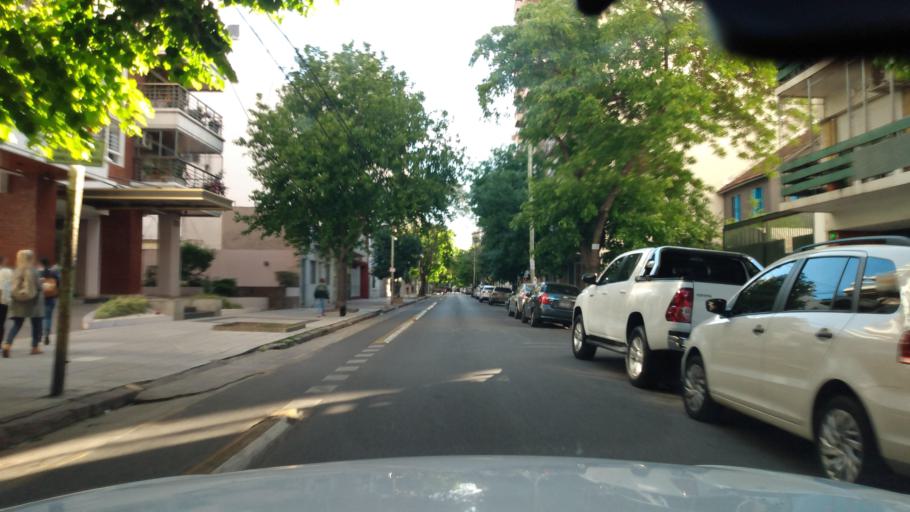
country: AR
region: Buenos Aires F.D.
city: Villa Santa Rita
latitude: -34.5766
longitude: -58.4881
